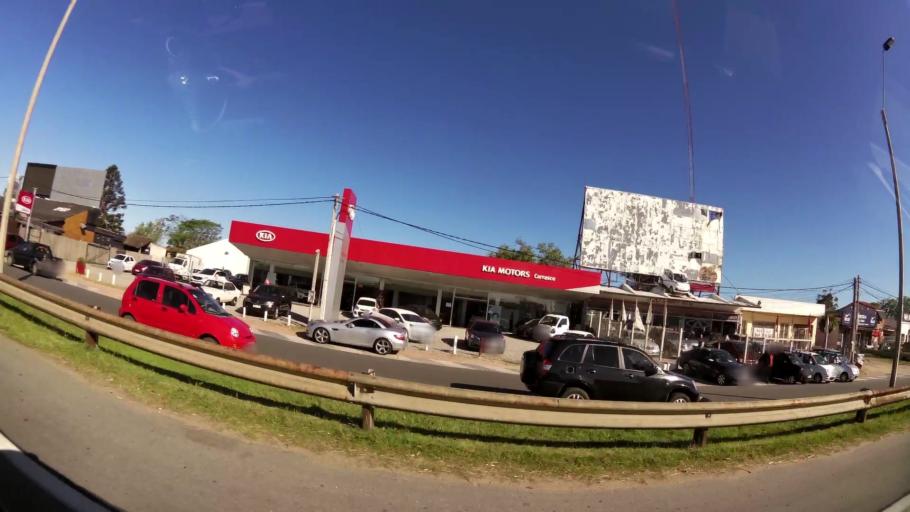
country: UY
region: Canelones
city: Barra de Carrasco
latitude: -34.8746
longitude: -56.0329
